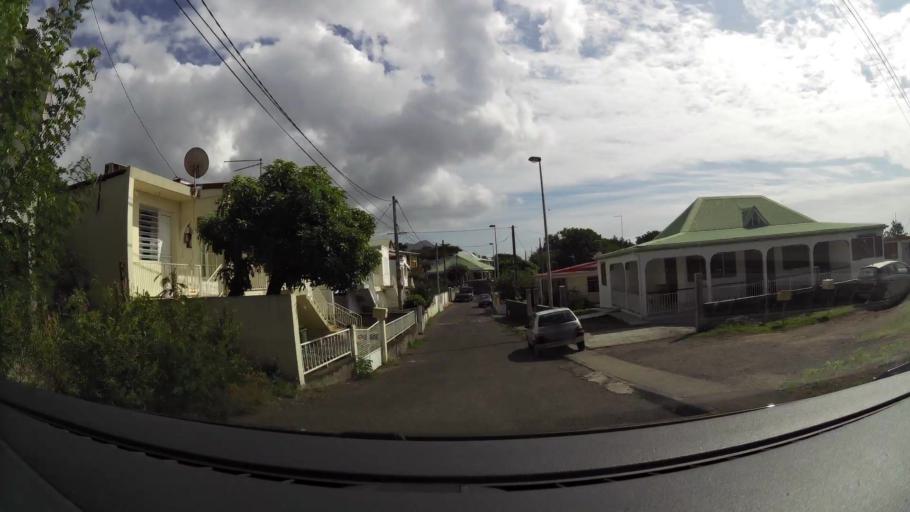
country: GP
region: Guadeloupe
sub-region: Guadeloupe
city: Basse-Terre
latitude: 16.0052
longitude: -61.7349
